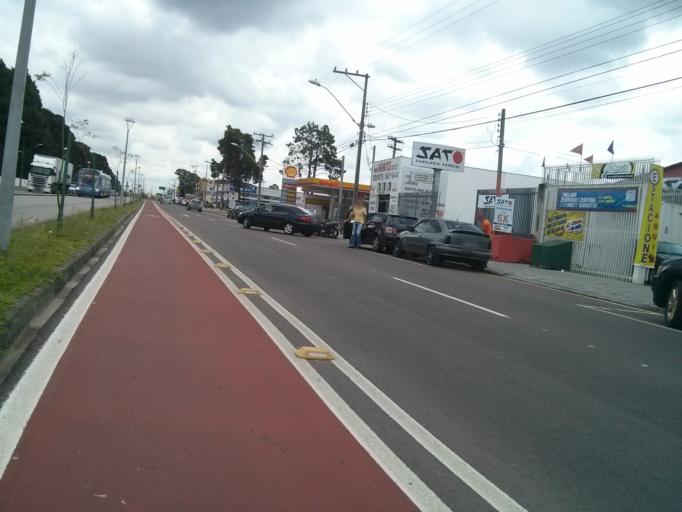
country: BR
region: Parana
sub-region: Sao Jose Dos Pinhais
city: Sao Jose dos Pinhais
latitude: -25.5095
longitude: -49.2335
